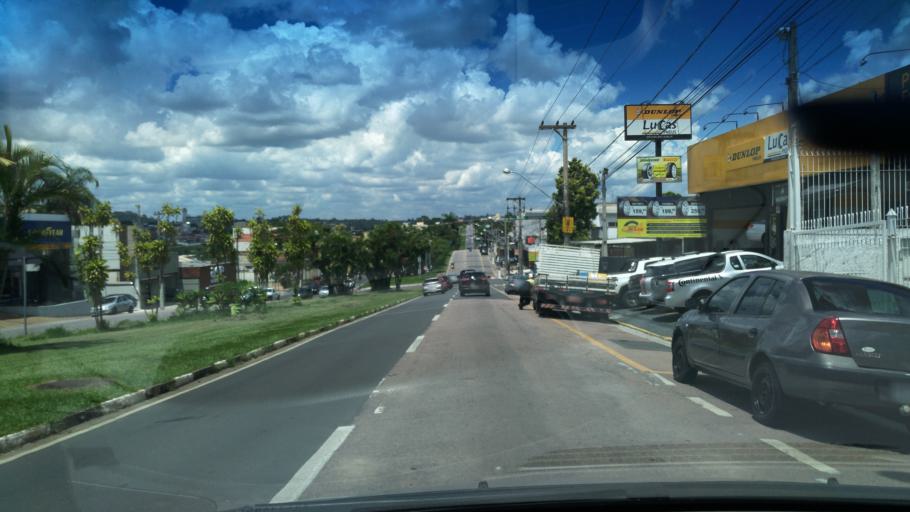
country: BR
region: Sao Paulo
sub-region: Vinhedo
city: Vinhedo
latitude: -23.0196
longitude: -46.9844
